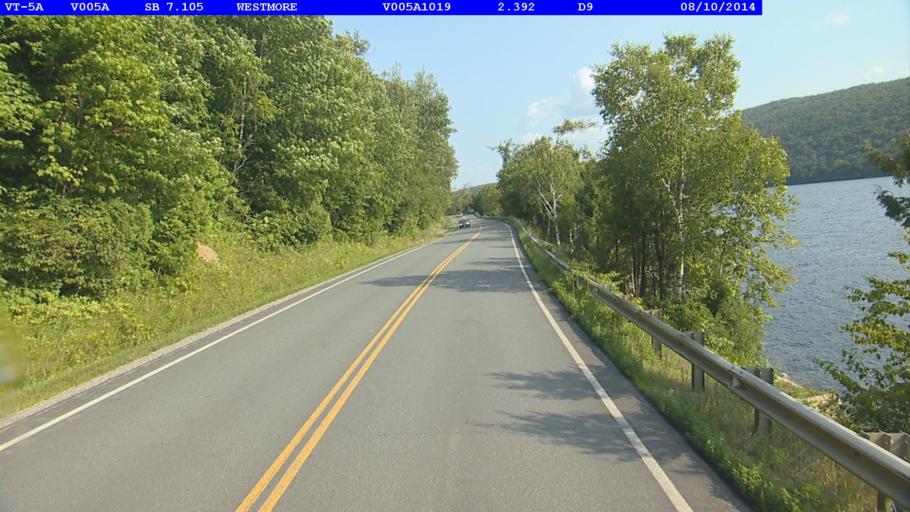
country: US
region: Vermont
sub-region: Caledonia County
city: Lyndonville
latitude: 44.7275
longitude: -72.0368
